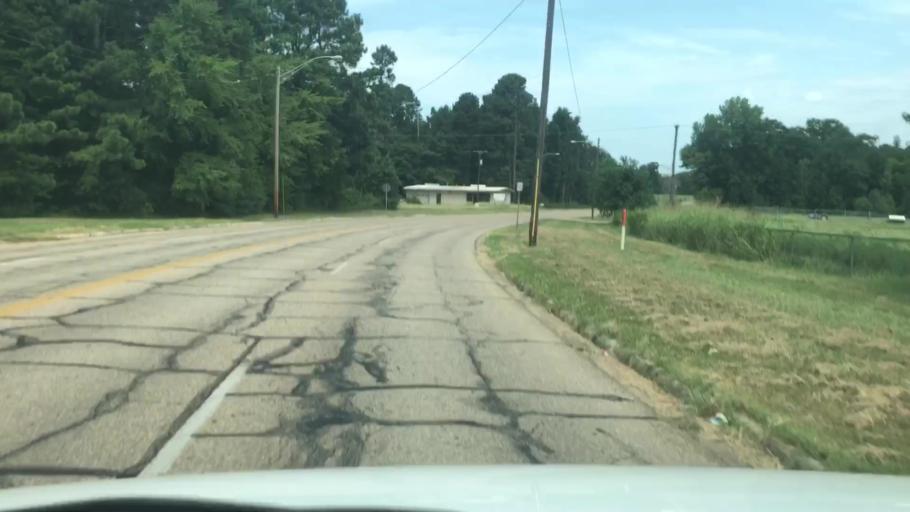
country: US
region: Texas
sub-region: Bowie County
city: Wake Village
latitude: 33.4087
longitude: -94.0800
